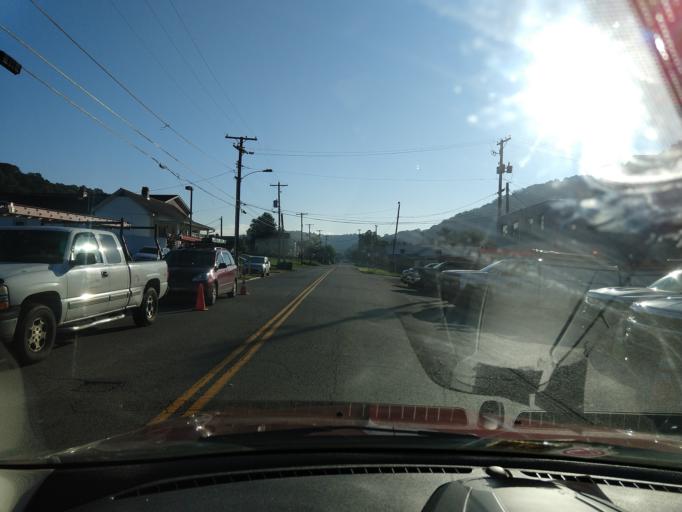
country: US
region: West Virginia
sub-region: Kanawha County
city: Charleston
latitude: 38.3612
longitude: -81.6200
